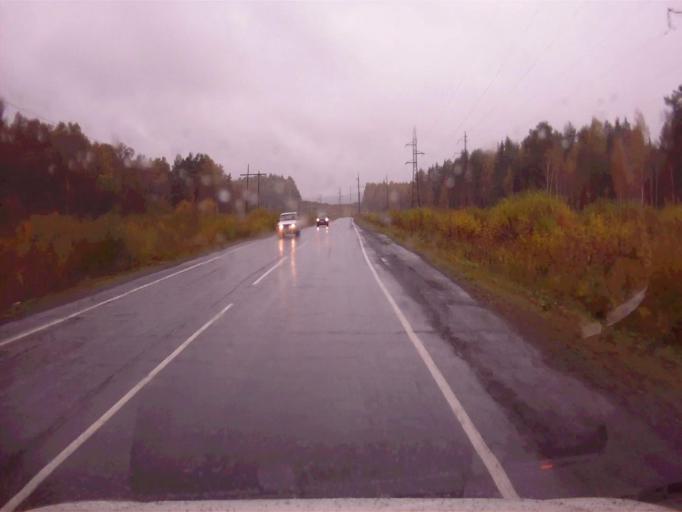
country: RU
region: Chelyabinsk
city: Verkhniy Ufaley
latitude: 55.9464
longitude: 60.4045
